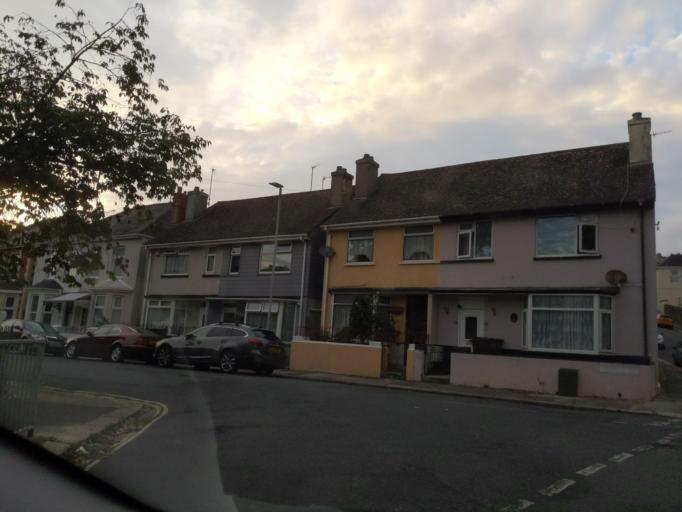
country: GB
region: England
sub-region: Cornwall
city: Millbrook
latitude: 50.3842
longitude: -4.1721
